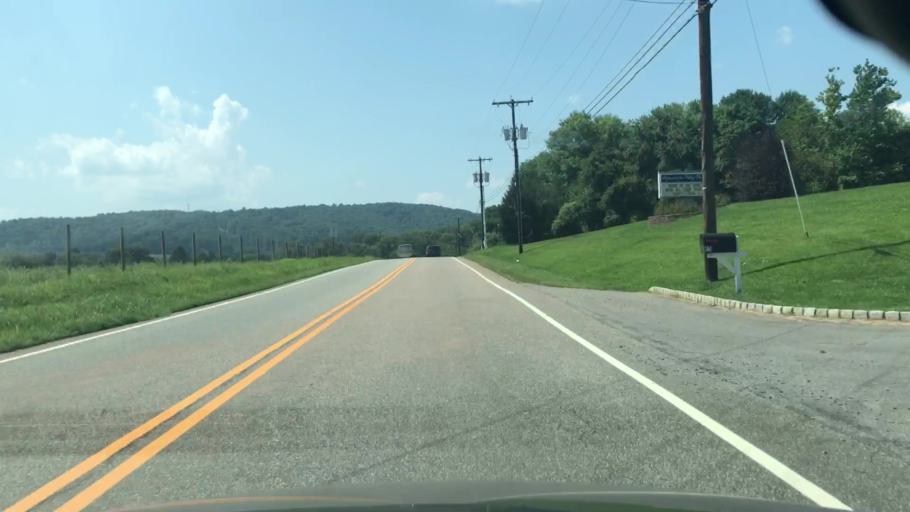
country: US
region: New Jersey
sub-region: Hunterdon County
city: Milford
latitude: 40.5952
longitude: -75.1127
